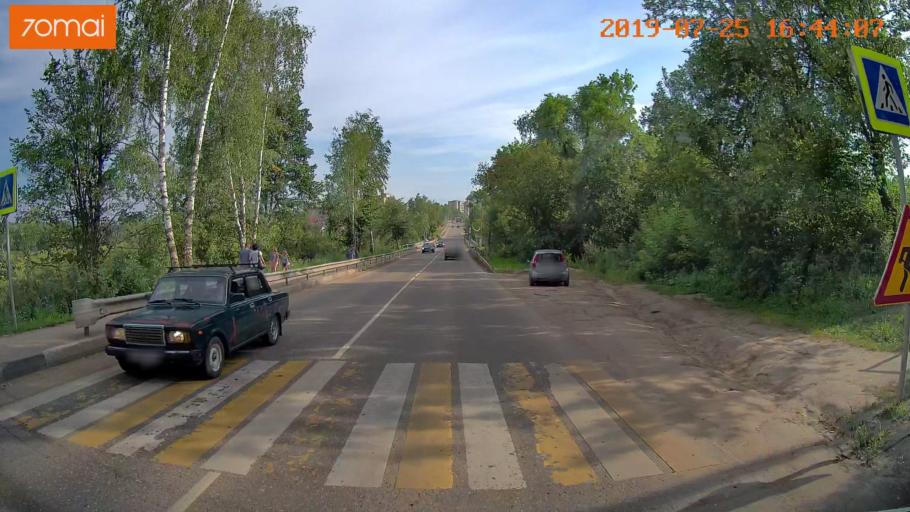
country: RU
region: Ivanovo
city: Privolzhsk
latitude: 57.3780
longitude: 41.2798
